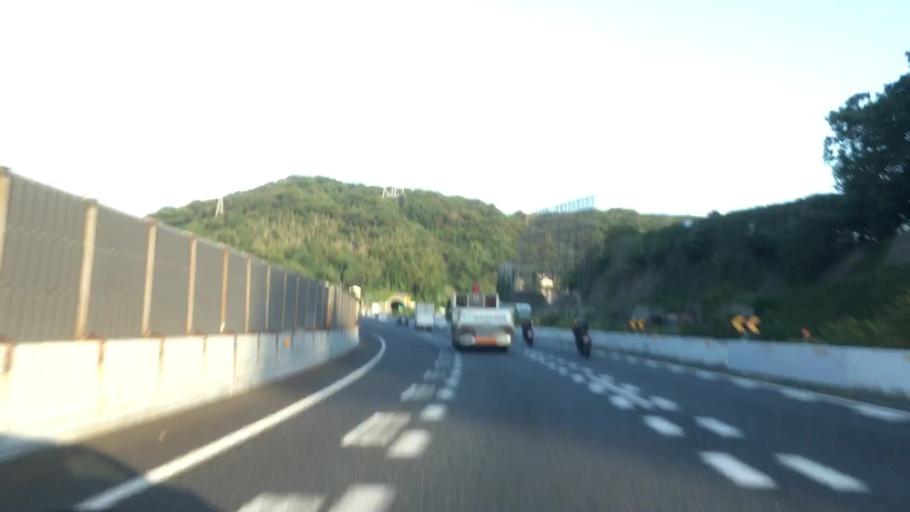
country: JP
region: Yamaguchi
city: Shimonoseki
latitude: 33.9543
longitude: 130.9743
